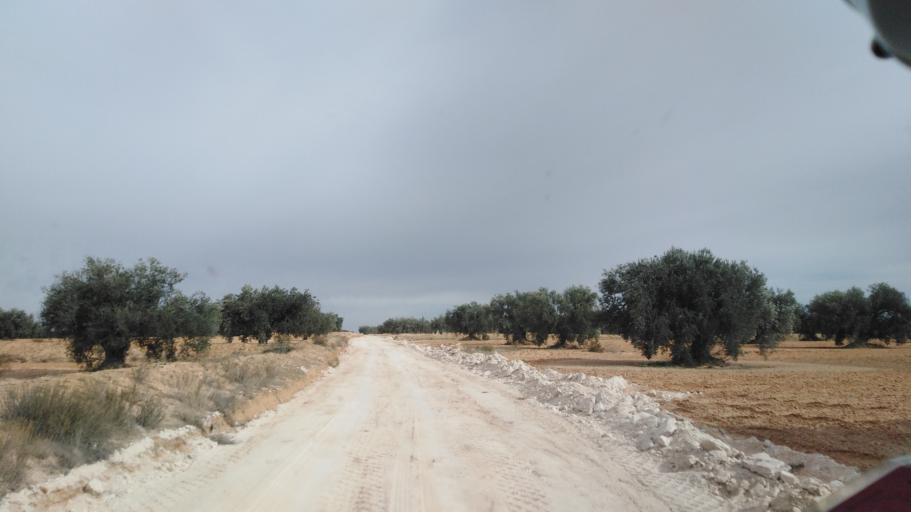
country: TN
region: Safaqis
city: Bi'r `Ali Bin Khalifah
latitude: 34.8111
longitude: 10.3057
